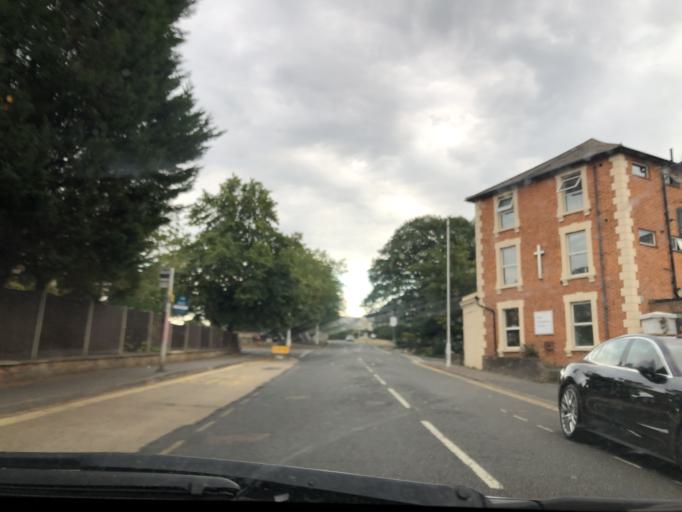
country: GB
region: England
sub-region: Kent
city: Sevenoaks
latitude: 51.2778
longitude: 0.1937
